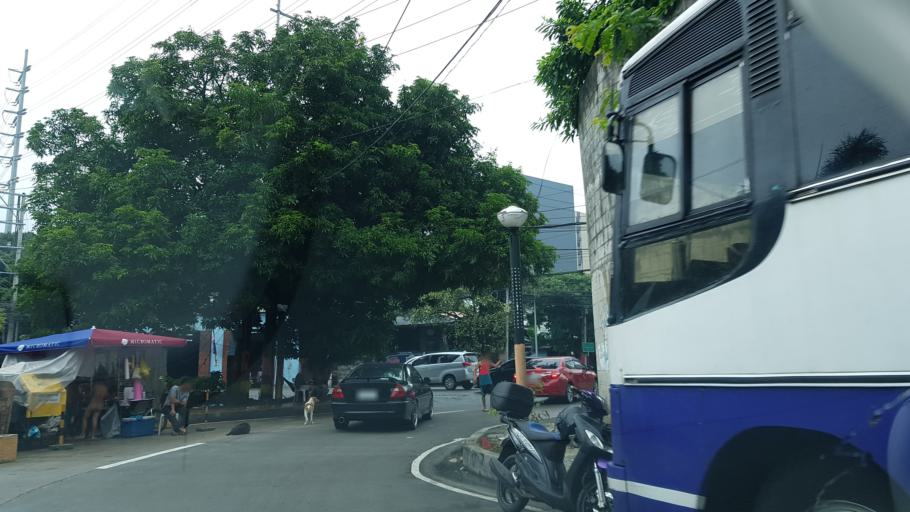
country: PH
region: Metro Manila
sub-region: City of Manila
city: Quiapo
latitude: 14.5813
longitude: 120.9882
